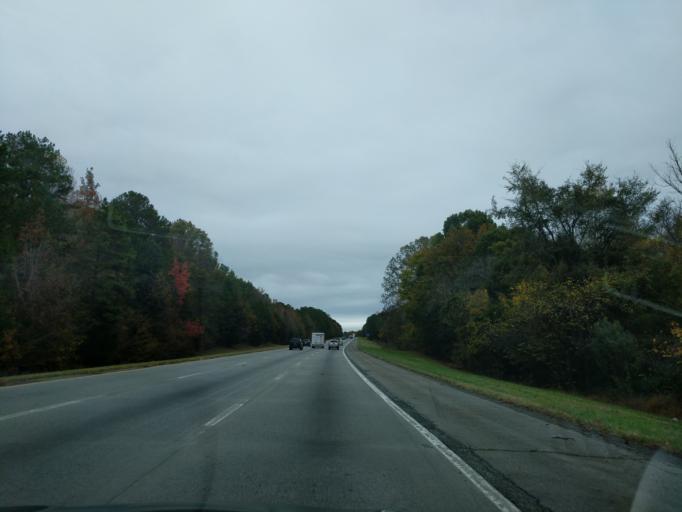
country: US
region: North Carolina
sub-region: Davidson County
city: Thomasville
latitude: 35.8297
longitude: -80.1579
